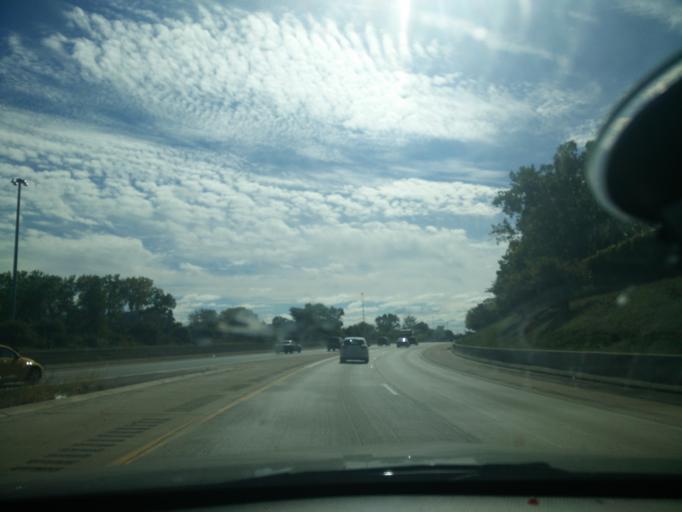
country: US
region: Michigan
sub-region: Macomb County
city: Roseville
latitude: 42.4924
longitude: -82.9173
